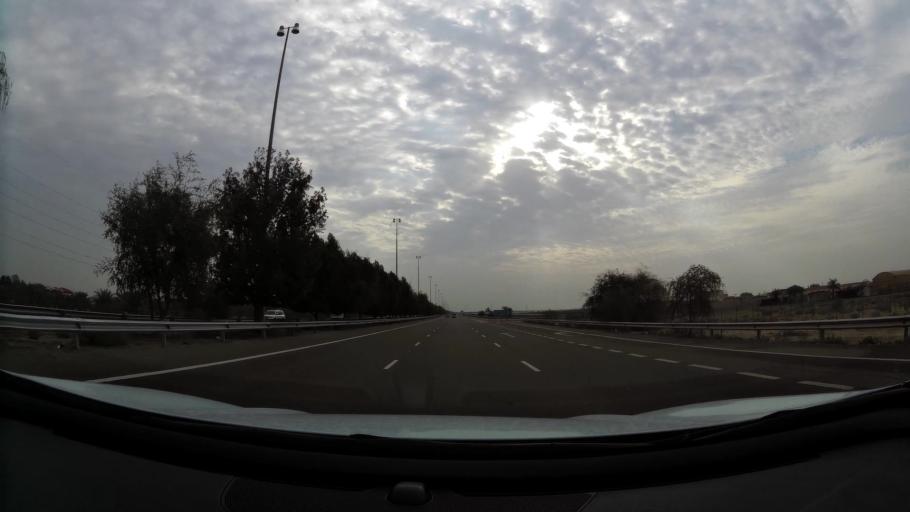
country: AE
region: Abu Dhabi
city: Abu Dhabi
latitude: 24.1895
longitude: 55.0142
